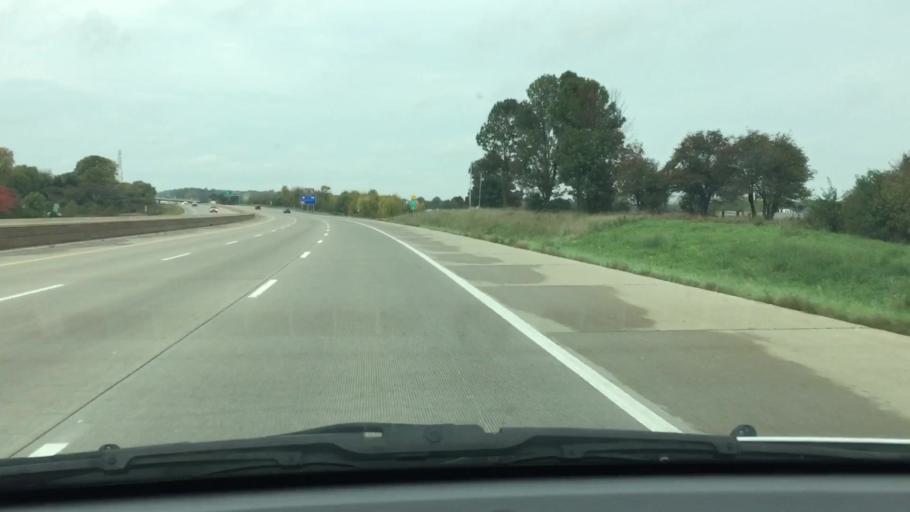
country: US
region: Iowa
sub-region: Johnson County
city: Iowa City
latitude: 41.6862
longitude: -91.4857
